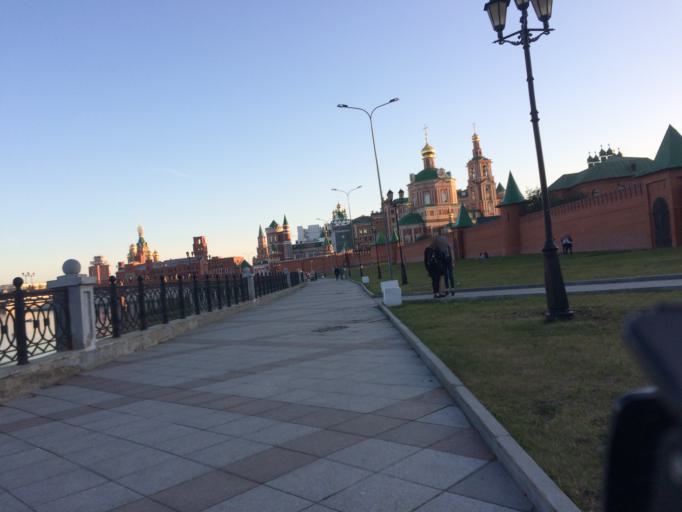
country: RU
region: Mariy-El
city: Yoshkar-Ola
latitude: 56.6386
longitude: 47.9045
